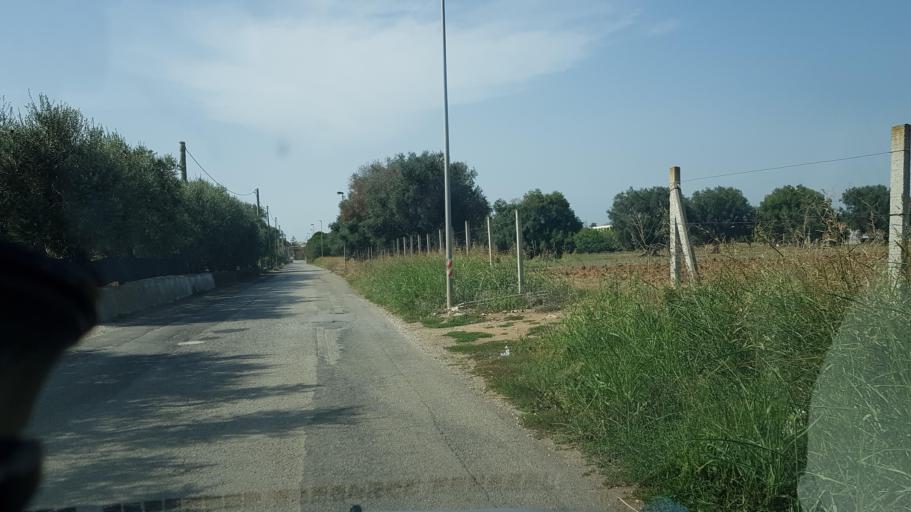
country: IT
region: Apulia
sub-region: Provincia di Brindisi
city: Mesagne
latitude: 40.5652
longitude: 17.8214
